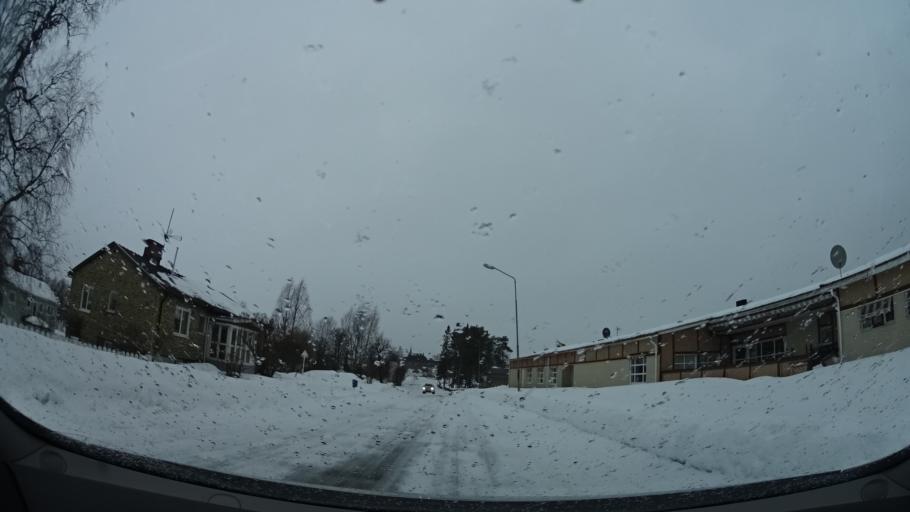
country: SE
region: Vaesterbotten
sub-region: Mala Kommun
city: Mala
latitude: 65.1810
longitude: 18.7462
